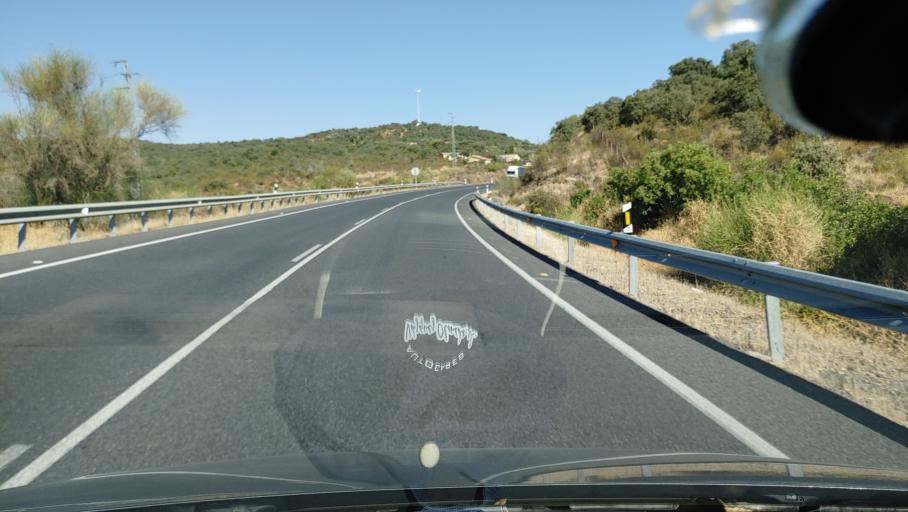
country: ES
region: Andalusia
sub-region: Province of Cordoba
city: Villaharta
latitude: 38.1033
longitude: -4.8782
